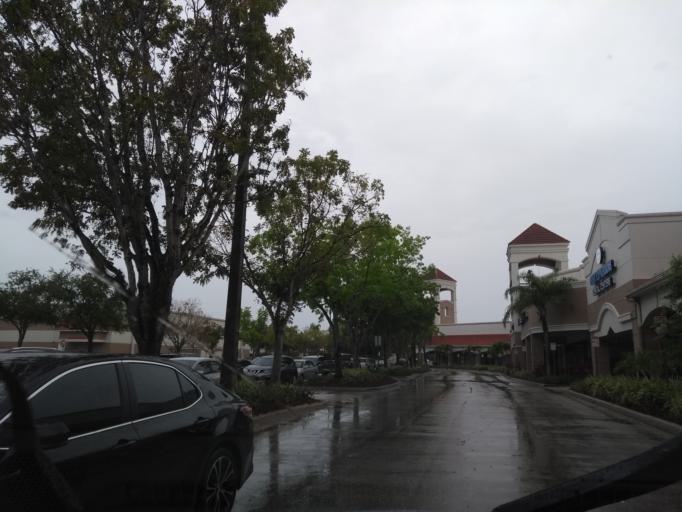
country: US
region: Florida
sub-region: Collier County
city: Pine Ridge
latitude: 26.2078
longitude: -81.7669
